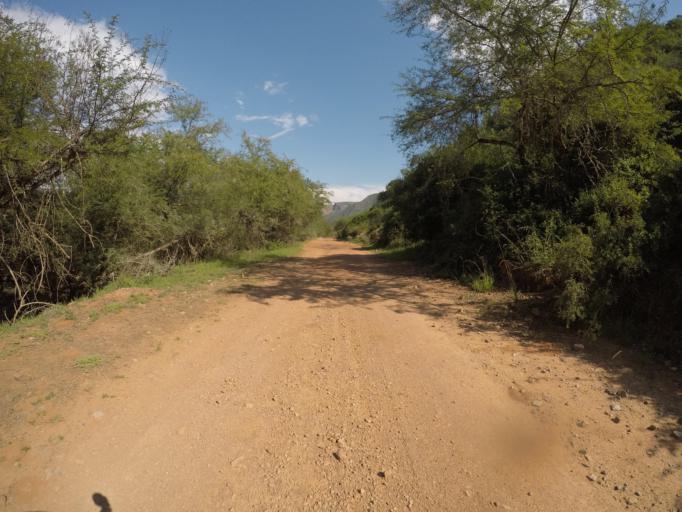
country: ZA
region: Eastern Cape
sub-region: Cacadu District Municipality
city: Kareedouw
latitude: -33.6613
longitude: 24.3951
